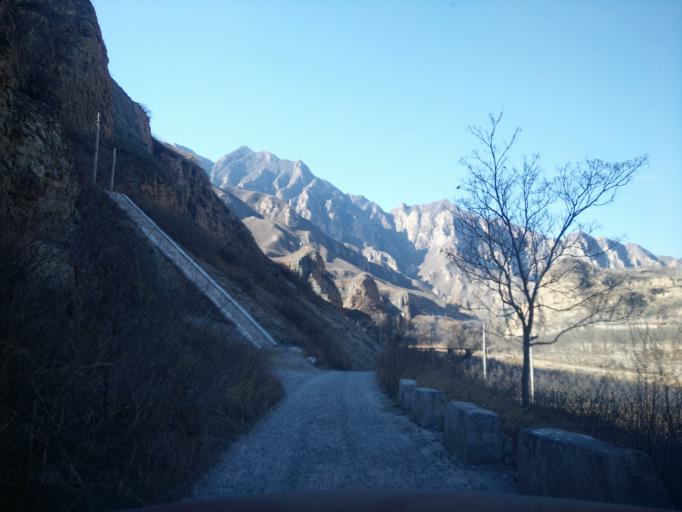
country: CN
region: Beijing
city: Yanjiatai
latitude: 40.1669
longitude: 115.6587
